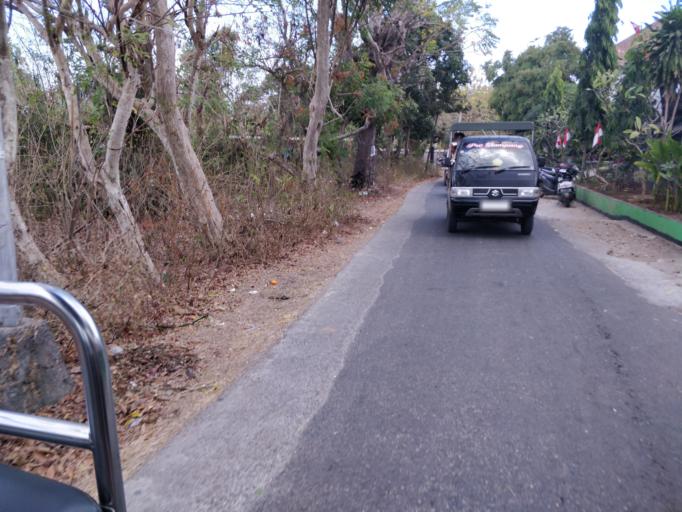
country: ID
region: Bali
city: Lembongan Kawan
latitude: -8.6858
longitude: 115.4436
